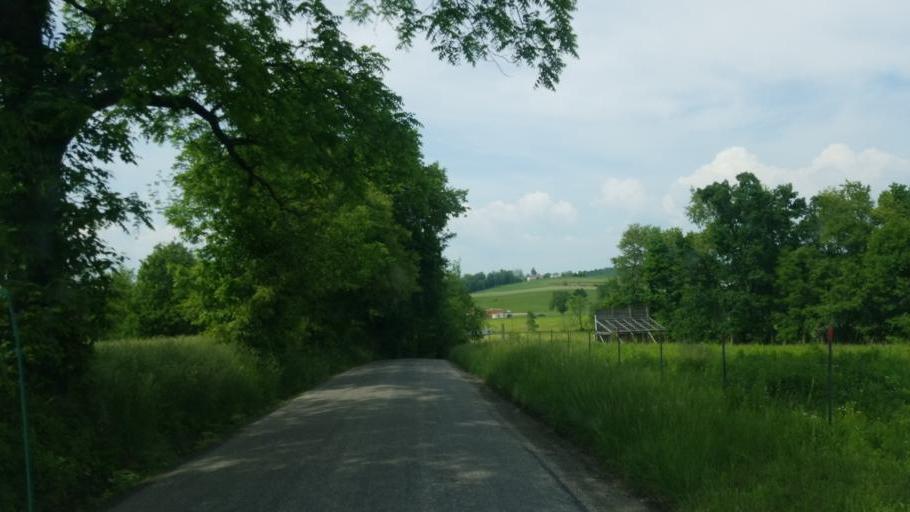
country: US
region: Ohio
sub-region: Holmes County
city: Millersburg
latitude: 40.5313
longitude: -81.8119
